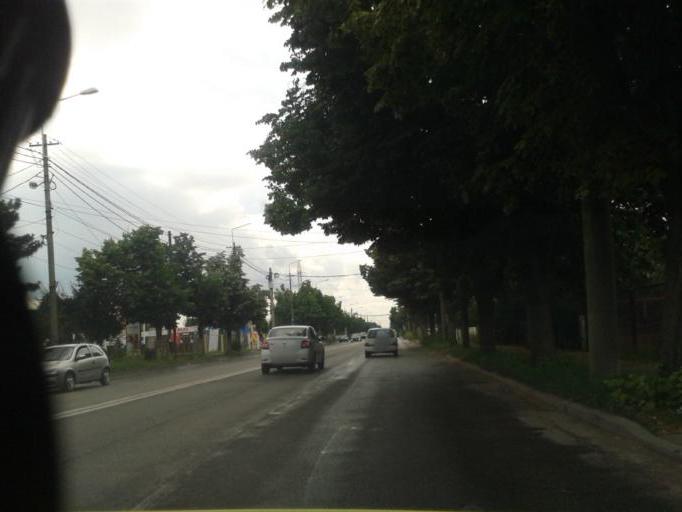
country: RO
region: Prahova
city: Ploiesti
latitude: 44.9601
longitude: 25.9812
